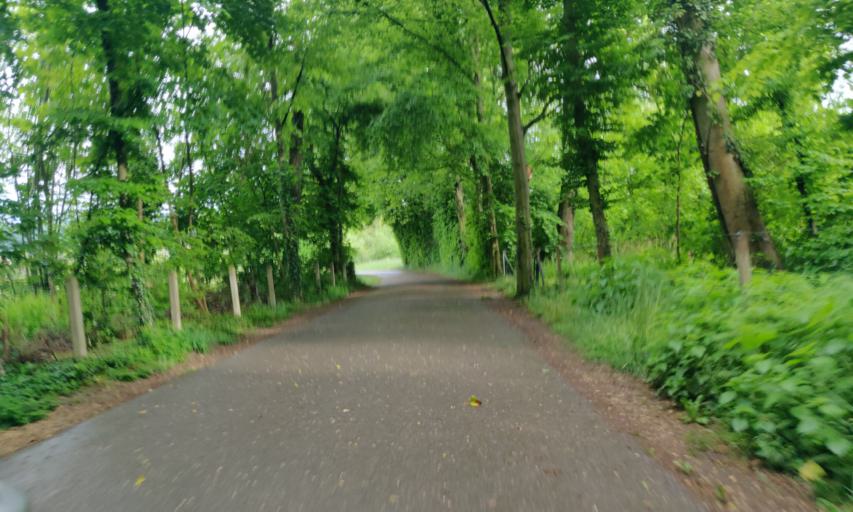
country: CH
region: Basel-City
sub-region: Basel-Stadt
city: Riehen
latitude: 47.5781
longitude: 7.6302
